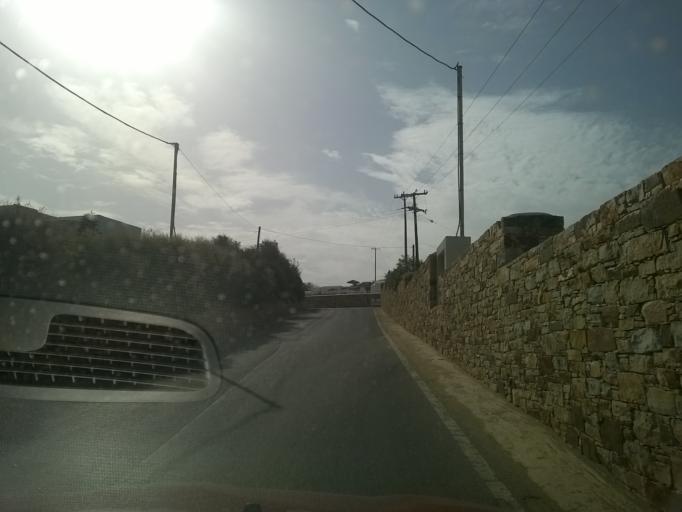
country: GR
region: South Aegean
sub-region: Nomos Kykladon
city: Naxos
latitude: 37.0847
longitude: 25.3491
